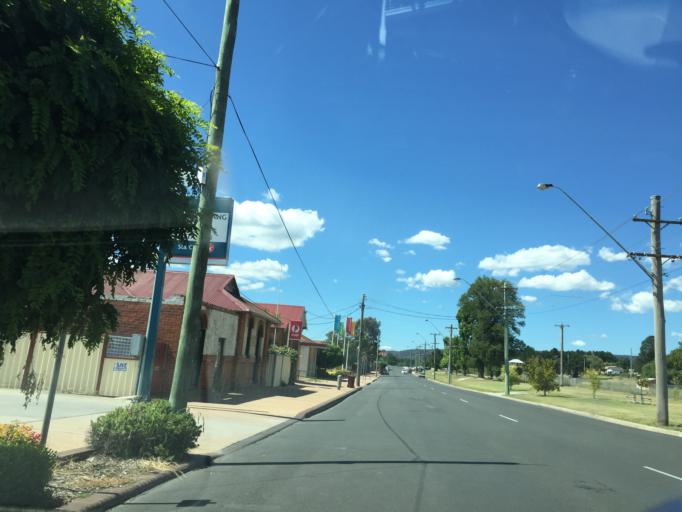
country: AU
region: New South Wales
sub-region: Lithgow
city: Portland
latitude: -33.4098
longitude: 150.0658
